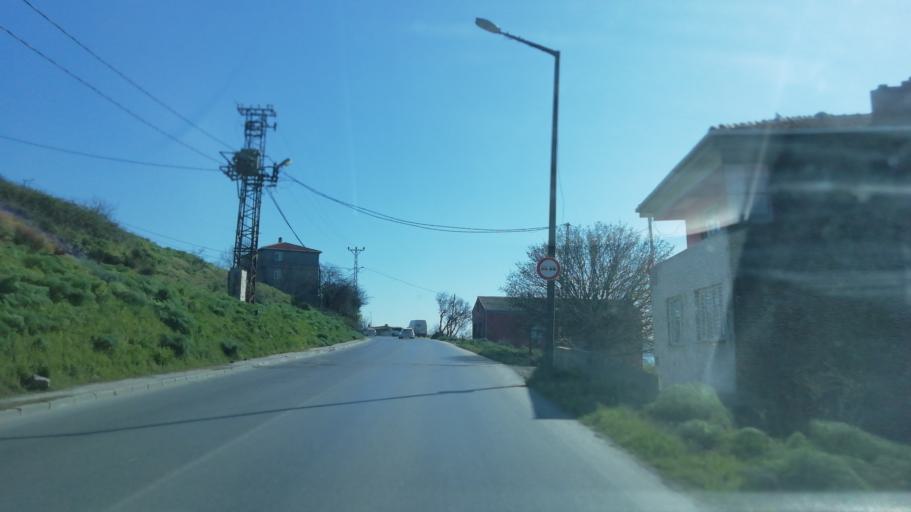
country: TR
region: Istanbul
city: Basaksehir
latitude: 41.0483
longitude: 28.7487
